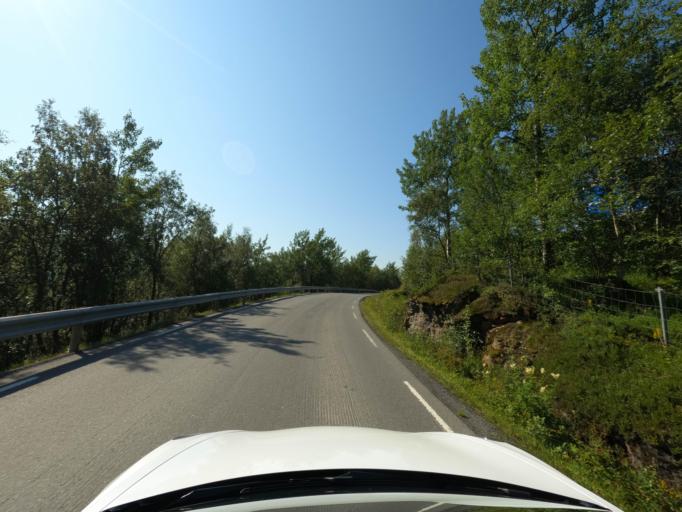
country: NO
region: Nordland
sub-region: Ballangen
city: Ballangen
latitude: 68.3580
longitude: 16.8739
